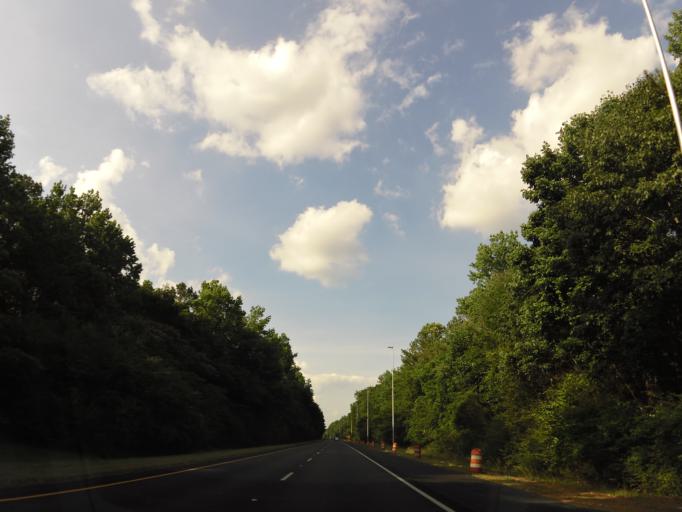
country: US
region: Alabama
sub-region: Jefferson County
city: Trussville
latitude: 33.6124
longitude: -86.6404
